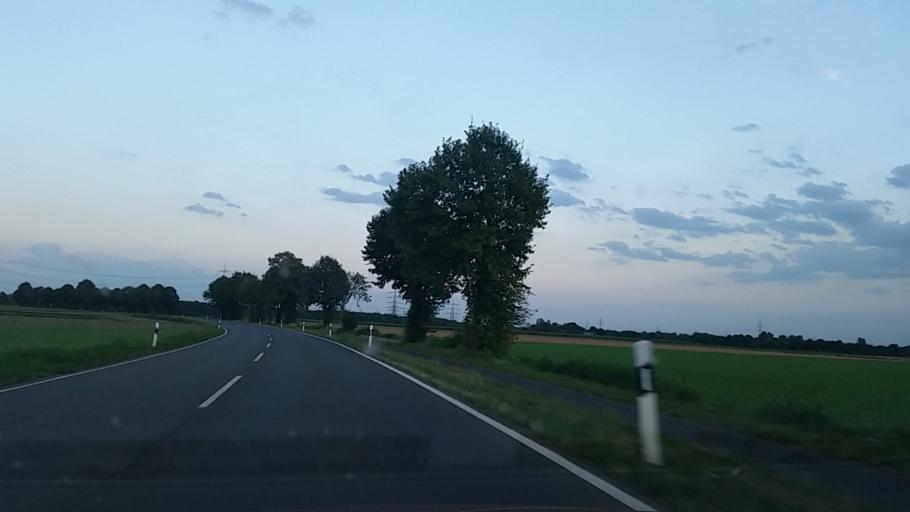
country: DE
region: North Rhine-Westphalia
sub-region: Regierungsbezirk Dusseldorf
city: Kaarst
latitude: 51.2663
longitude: 6.5942
